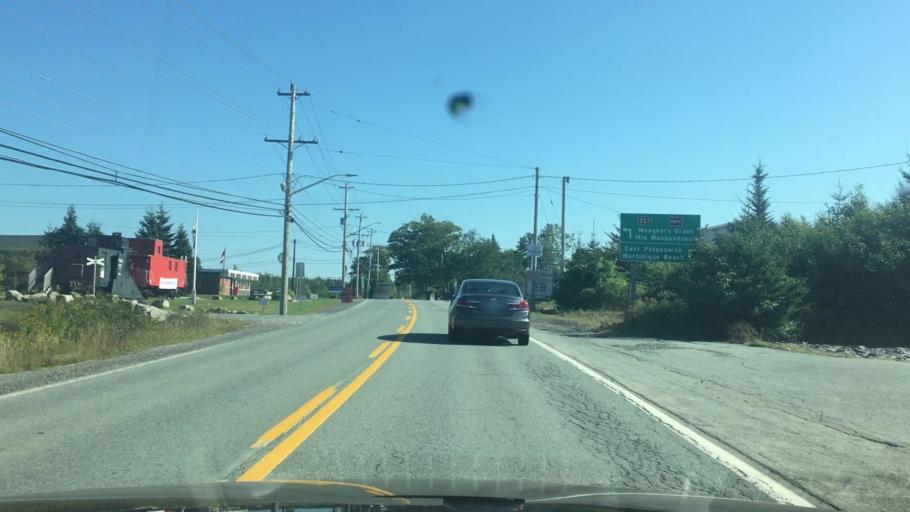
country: CA
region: Nova Scotia
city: Cole Harbour
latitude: 44.7857
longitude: -63.1497
